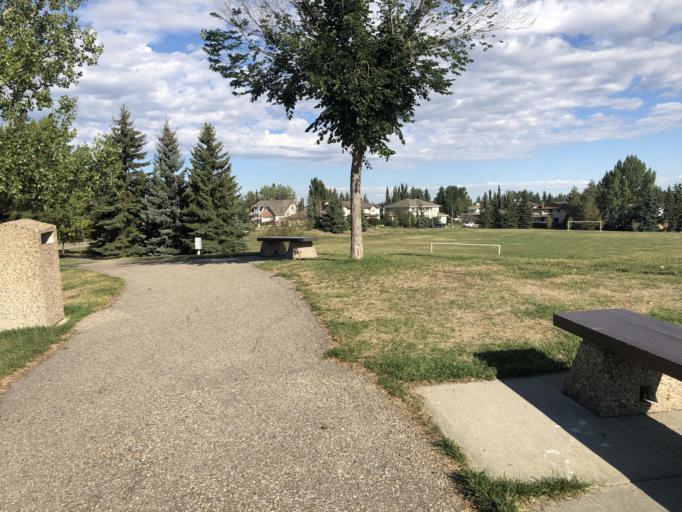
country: CA
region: Alberta
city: Edmonton
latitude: 53.4820
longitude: -113.5838
